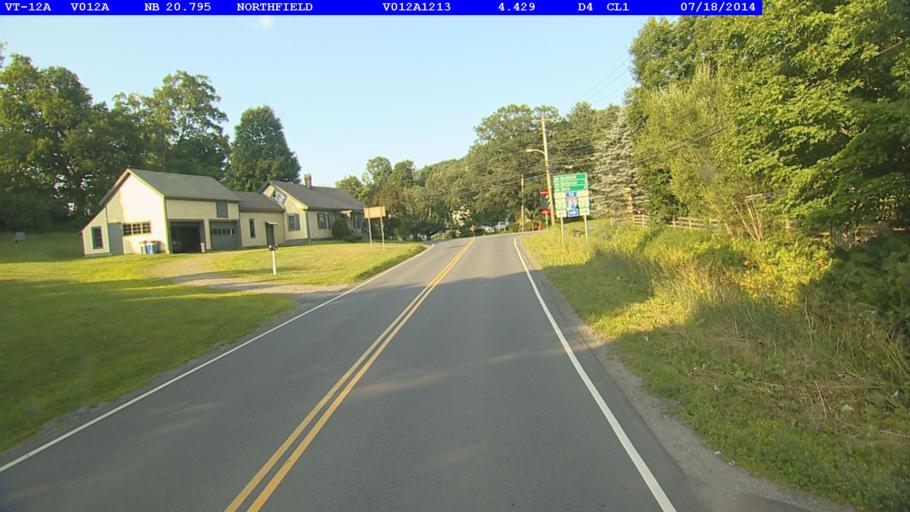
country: US
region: Vermont
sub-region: Washington County
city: Northfield
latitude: 44.1339
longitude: -72.6603
